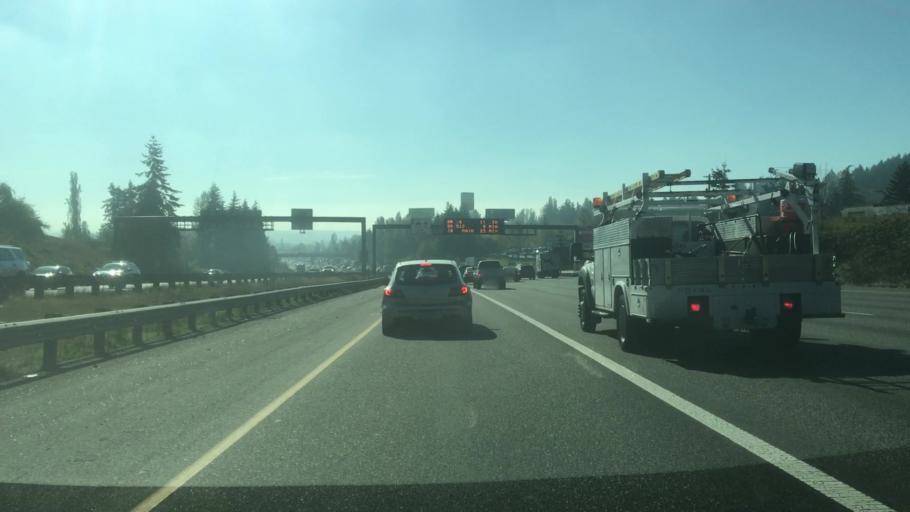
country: US
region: Washington
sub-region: Pierce County
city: Fife Heights
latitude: 47.2569
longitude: -122.3306
